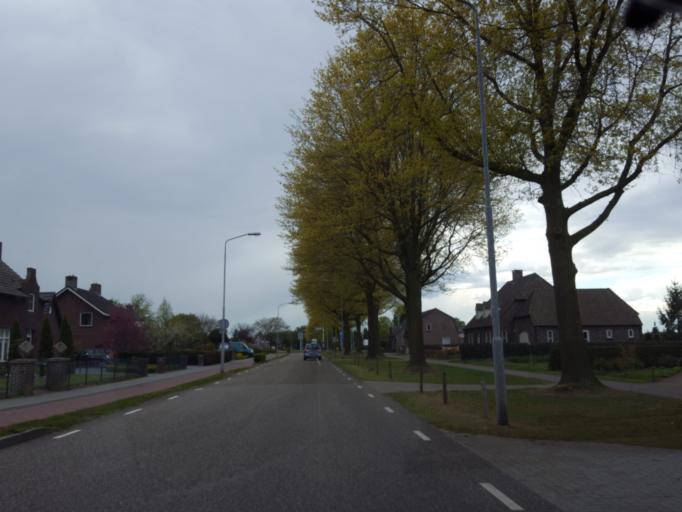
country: NL
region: North Brabant
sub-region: Gemeente Asten
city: Asten
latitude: 51.4512
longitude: 5.7773
